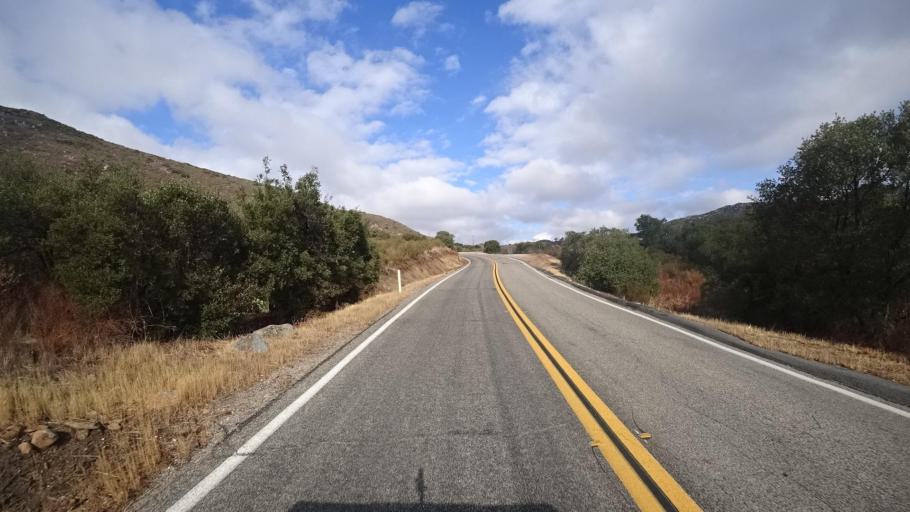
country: MX
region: Baja California
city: Tecate
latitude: 32.6234
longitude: -116.6220
